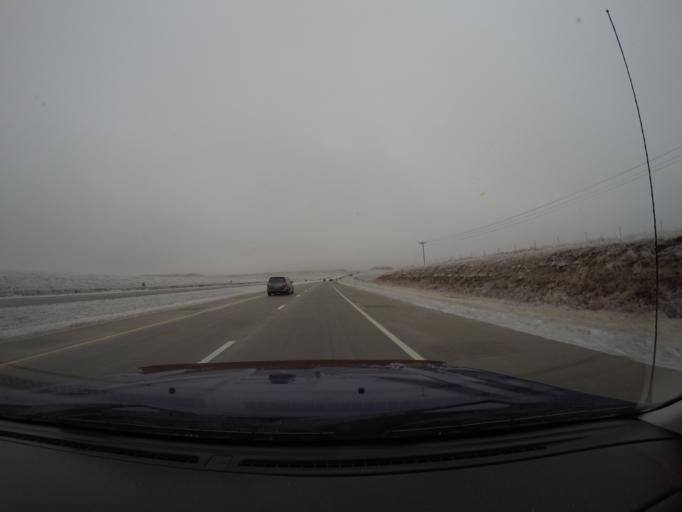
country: US
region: Kansas
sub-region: Riley County
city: Manhattan
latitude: 39.0637
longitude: -96.5163
